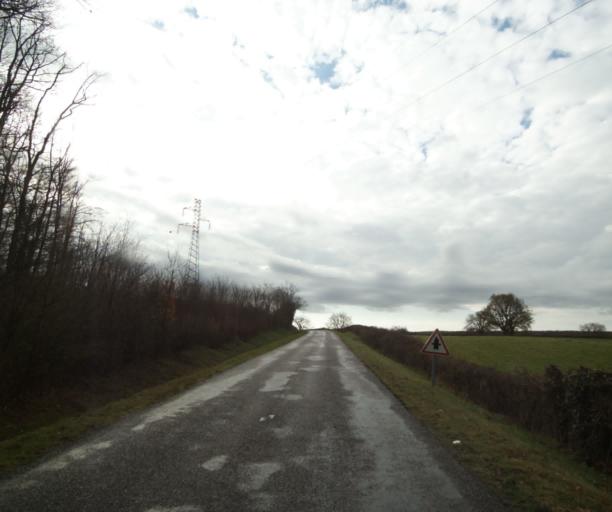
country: FR
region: Auvergne
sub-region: Departement de l'Allier
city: Neuilly-le-Real
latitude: 46.5215
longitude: 3.4199
